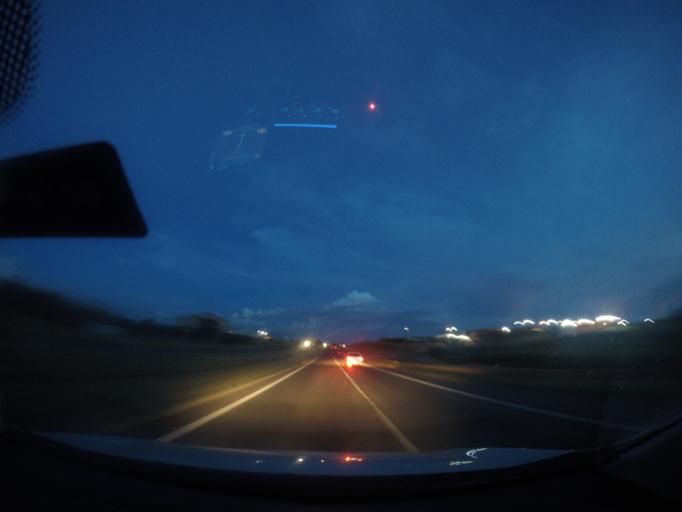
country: BR
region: Sao Paulo
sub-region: Cordeiropolis
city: Cordeiropolis
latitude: -22.4959
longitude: -47.4220
